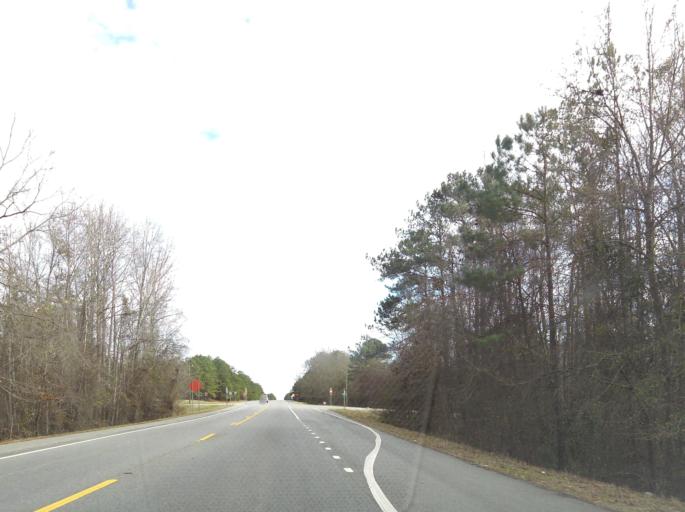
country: US
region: Georgia
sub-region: Bibb County
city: West Point
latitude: 32.7999
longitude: -83.7961
